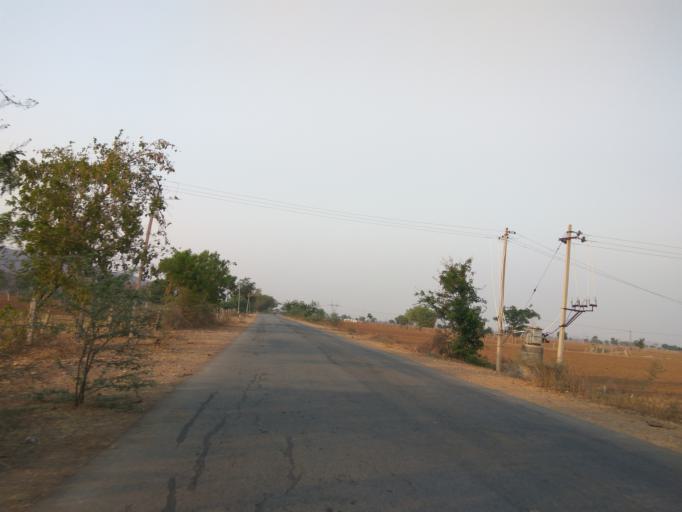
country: IN
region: Andhra Pradesh
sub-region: Prakasam
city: Cumbum
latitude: 15.6462
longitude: 79.1454
